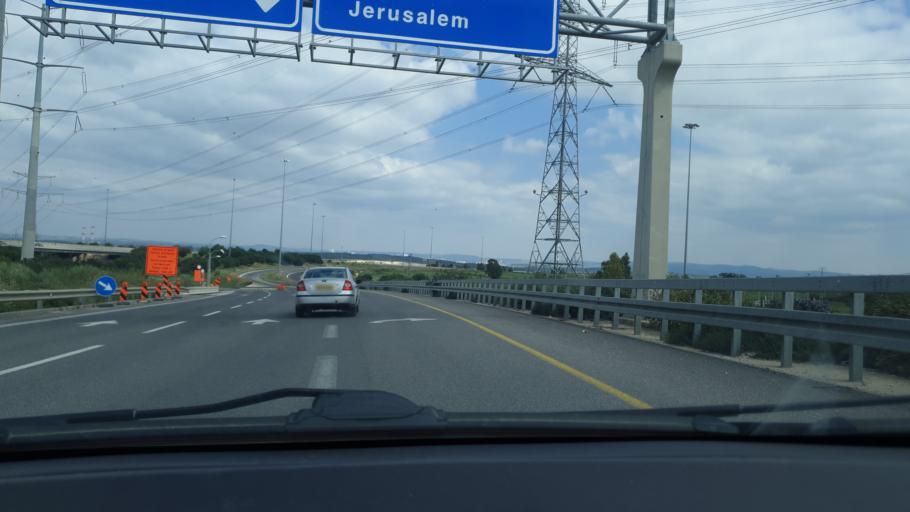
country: IL
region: Central District
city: Ramla
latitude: 31.9087
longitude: 34.8962
